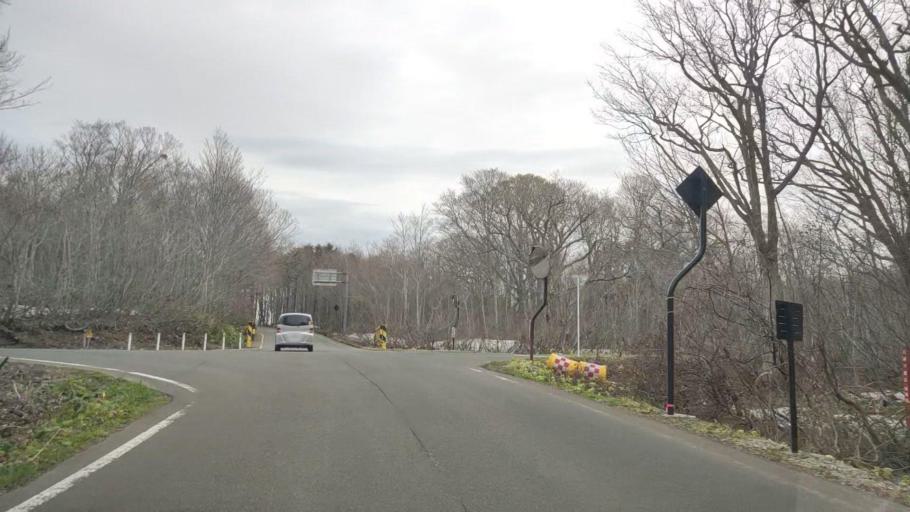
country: JP
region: Aomori
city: Aomori Shi
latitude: 40.6642
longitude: 140.9579
